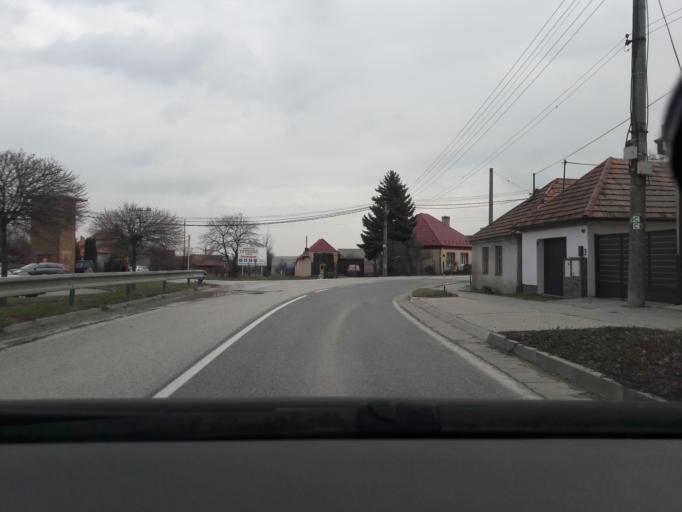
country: SK
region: Trnavsky
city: Smolenice
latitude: 48.4144
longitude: 17.3807
